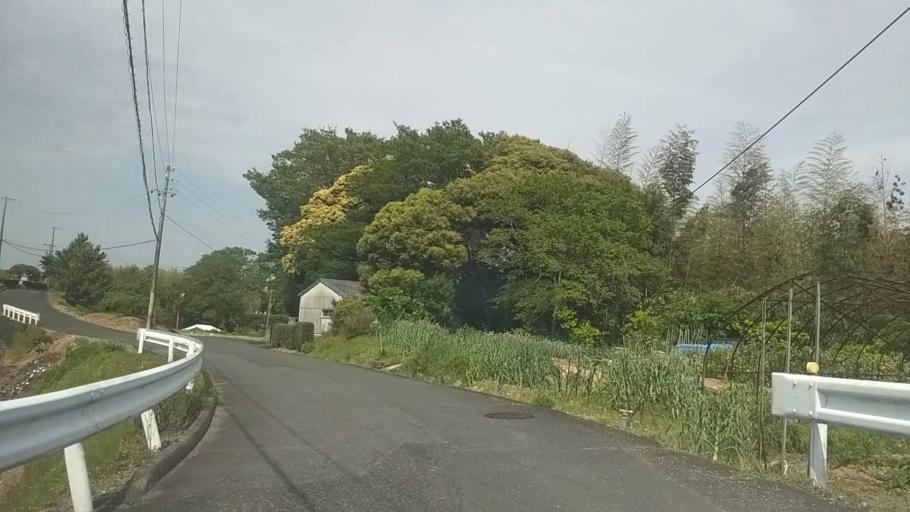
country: JP
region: Shizuoka
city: Kosai-shi
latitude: 34.7709
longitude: 137.6263
